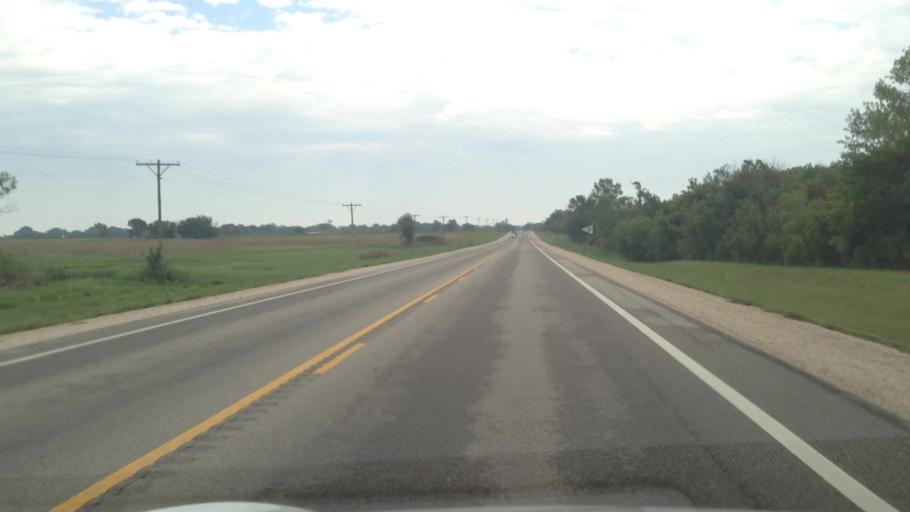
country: US
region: Kansas
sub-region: Allen County
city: Iola
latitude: 37.9033
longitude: -95.0899
